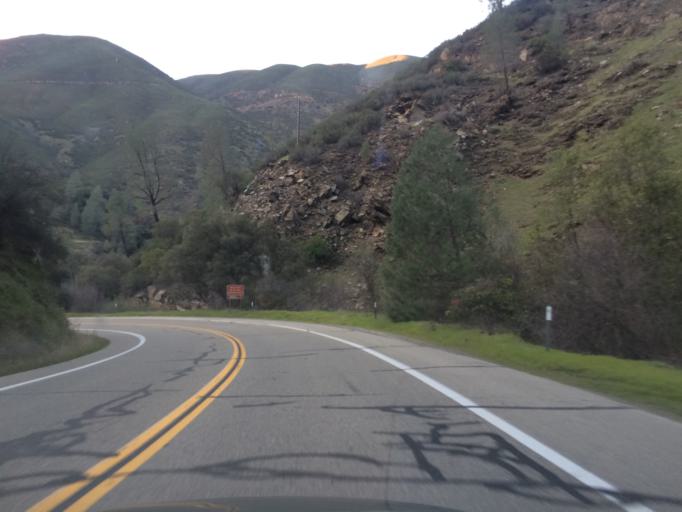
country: US
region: California
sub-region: Mariposa County
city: Midpines
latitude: 37.6034
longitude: -119.9640
